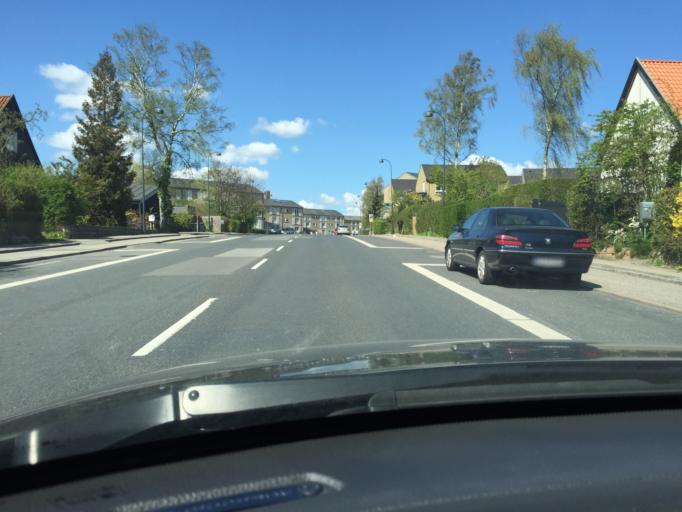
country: DK
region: Capital Region
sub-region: Lyngby-Tarbaek Kommune
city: Kongens Lyngby
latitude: 55.7596
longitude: 12.5288
